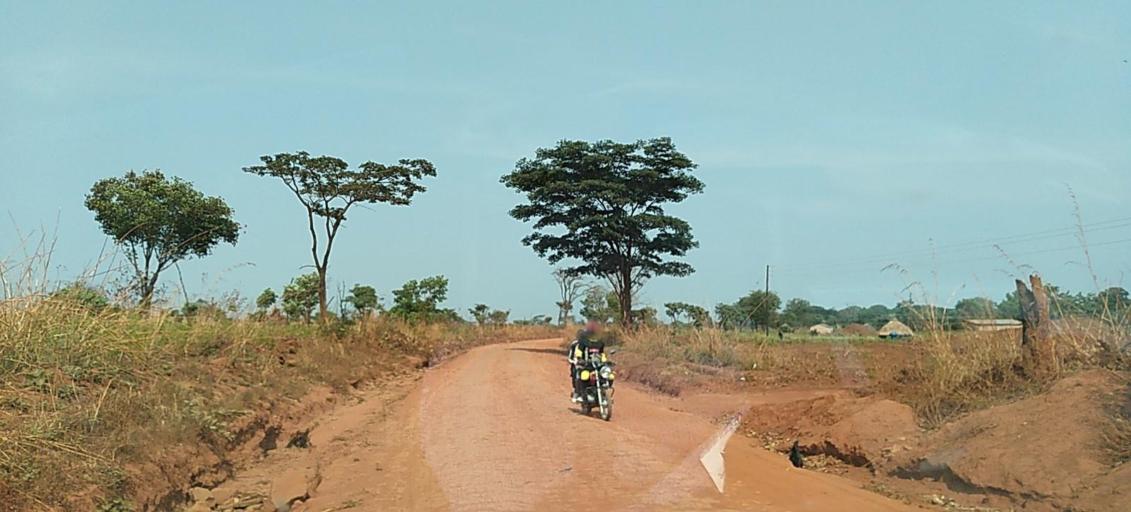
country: ZM
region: Copperbelt
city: Chililabombwe
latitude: -12.3425
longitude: 27.7024
